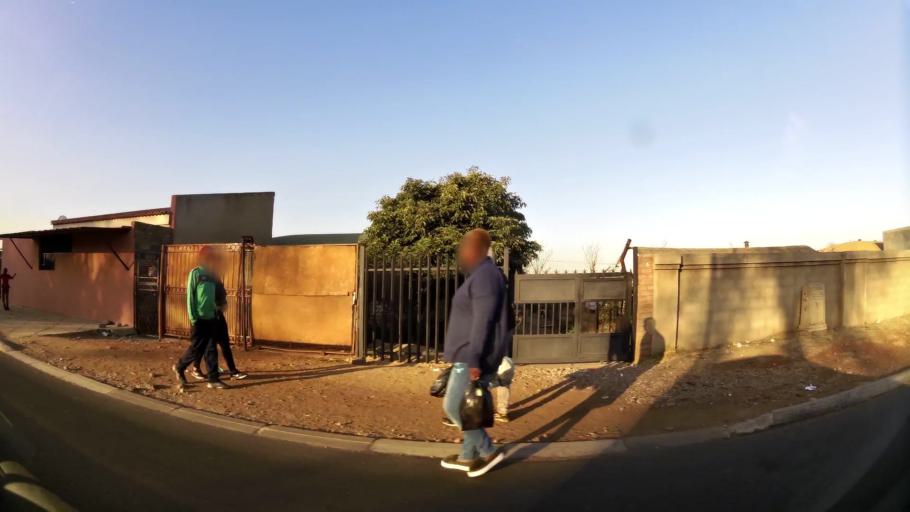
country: ZA
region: Gauteng
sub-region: City of Johannesburg Metropolitan Municipality
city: Soweto
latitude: -26.2495
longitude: 27.8777
